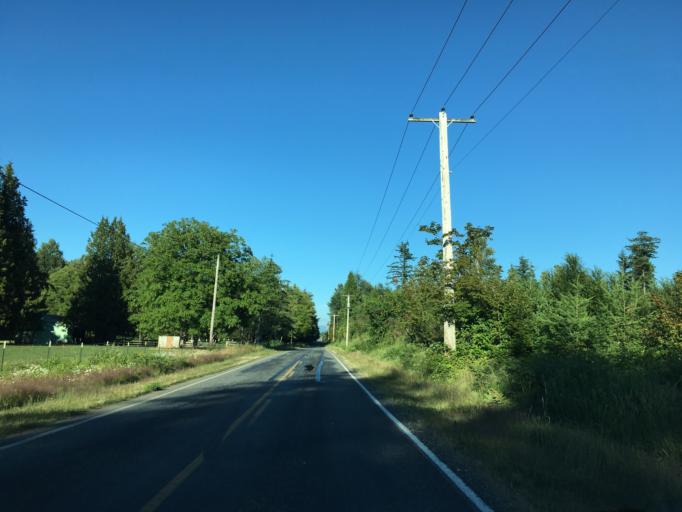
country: US
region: Washington
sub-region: Whatcom County
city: Ferndale
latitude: 48.9135
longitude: -122.6254
